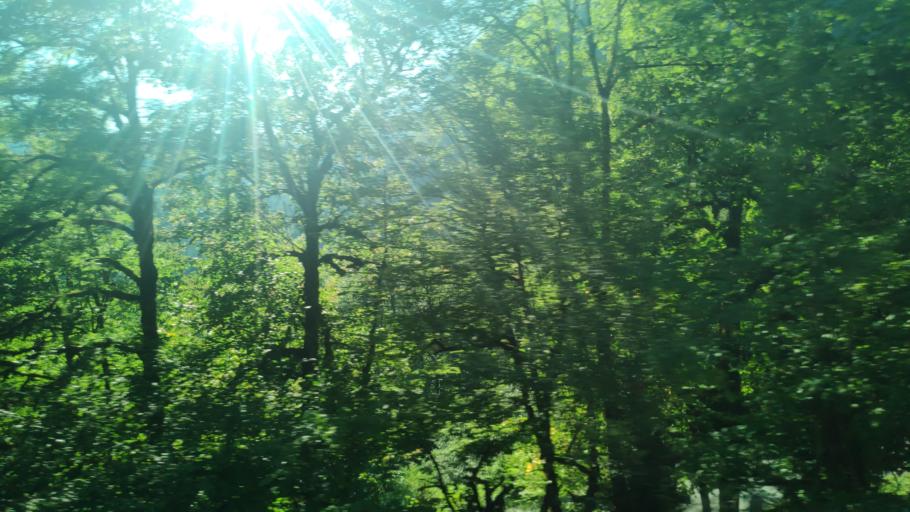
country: GE
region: Abkhazia
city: Gagra
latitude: 43.4530
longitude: 40.5453
